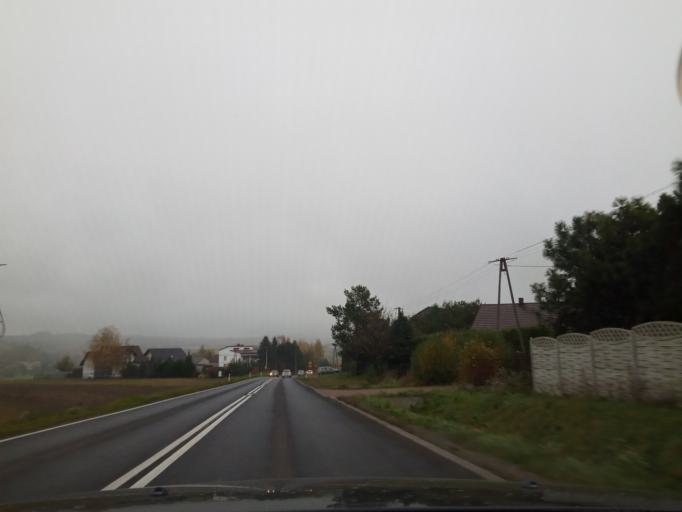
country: PL
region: Lesser Poland Voivodeship
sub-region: Powiat proszowicki
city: Proszowice
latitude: 50.1607
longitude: 20.2014
